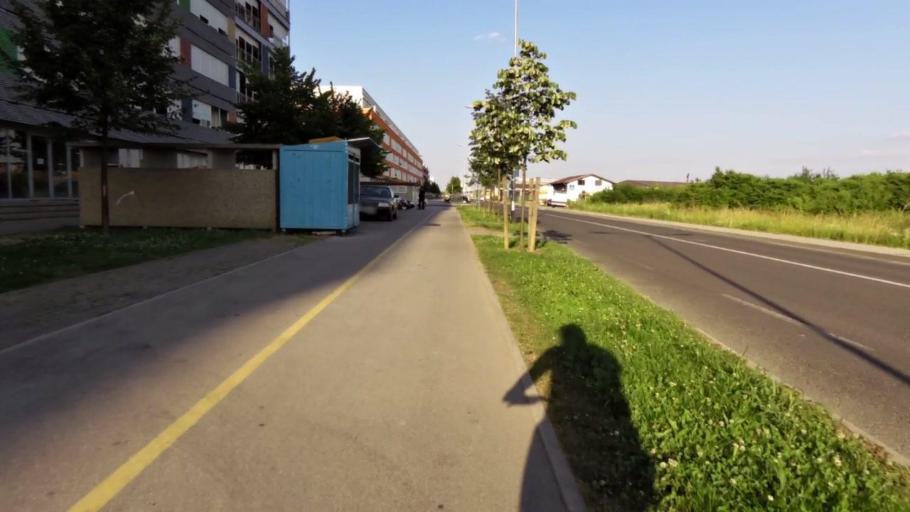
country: HR
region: Grad Zagreb
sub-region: Sesvete
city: Sesvete
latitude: 45.8099
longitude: 16.1027
